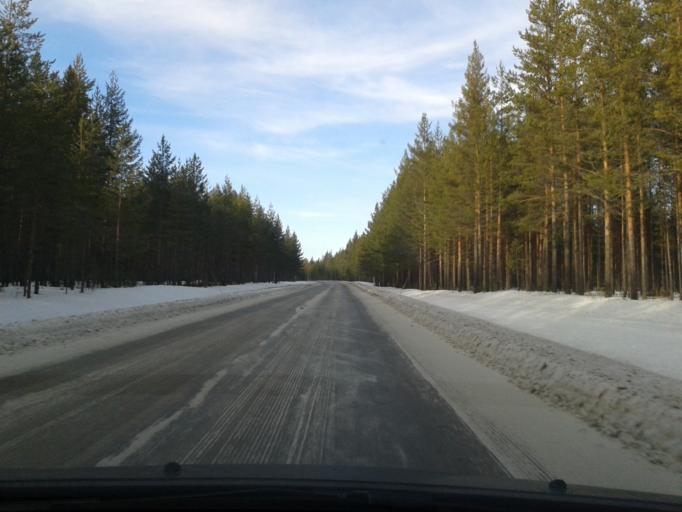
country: SE
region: Vaesternorrland
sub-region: OErnskoeldsviks Kommun
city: Bredbyn
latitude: 63.5339
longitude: 17.9666
